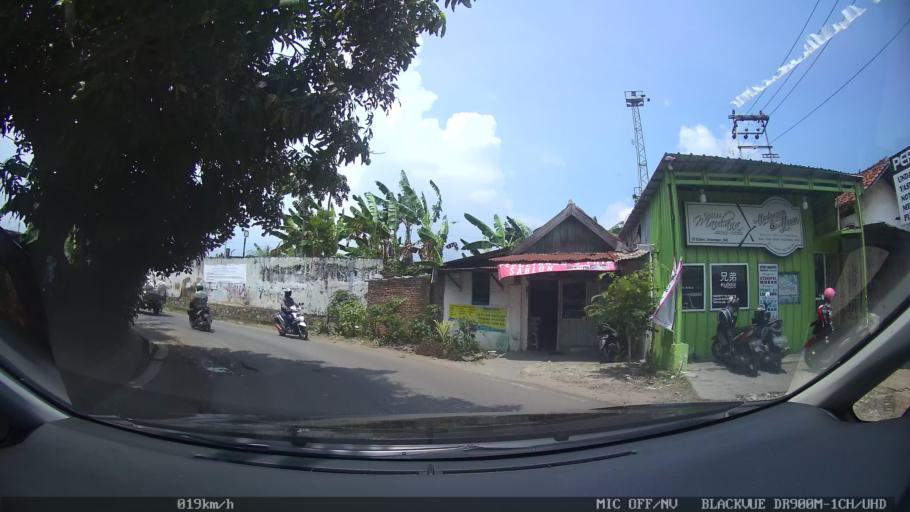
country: ID
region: Lampung
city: Bandarlampung
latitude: -5.4046
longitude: 105.2604
